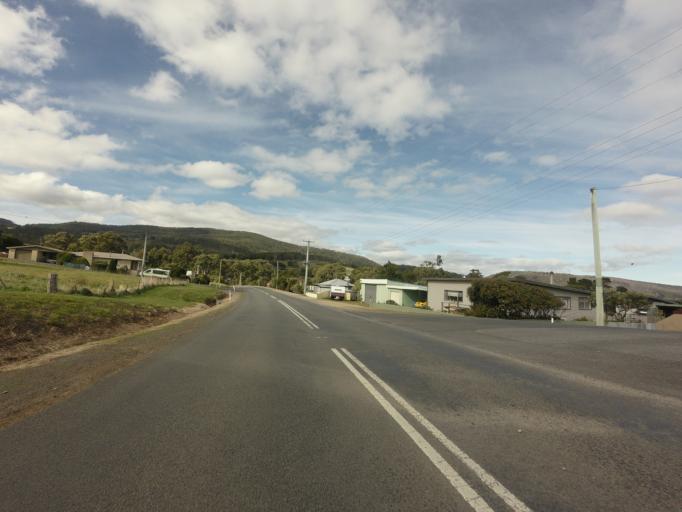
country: AU
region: Tasmania
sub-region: Clarence
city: Sandford
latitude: -43.0938
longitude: 147.7402
